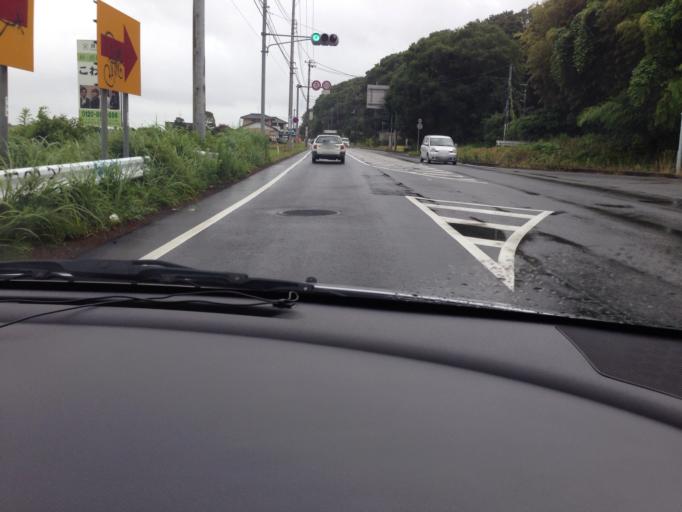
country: JP
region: Ibaraki
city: Ami
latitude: 36.0318
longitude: 140.2599
